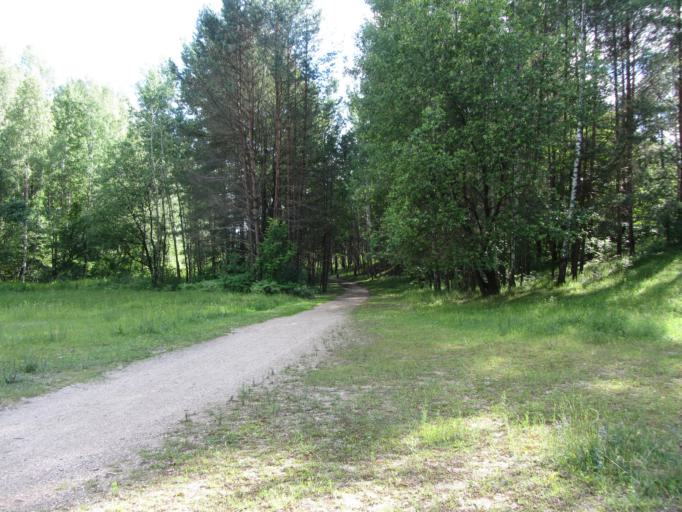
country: LT
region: Vilnius County
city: Lazdynai
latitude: 54.6783
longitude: 25.1975
